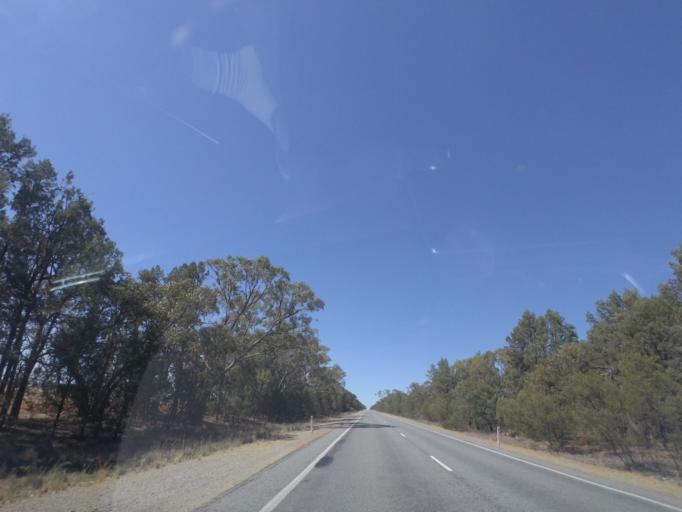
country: AU
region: New South Wales
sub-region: Narrandera
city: Narrandera
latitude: -34.4259
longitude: 146.8441
